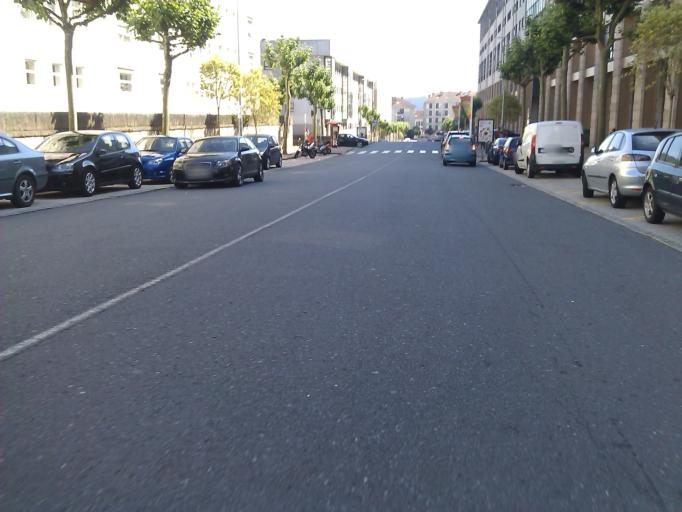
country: ES
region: Galicia
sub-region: Provincia da Coruna
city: Santiago de Compostela
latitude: 42.8830
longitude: -8.5261
